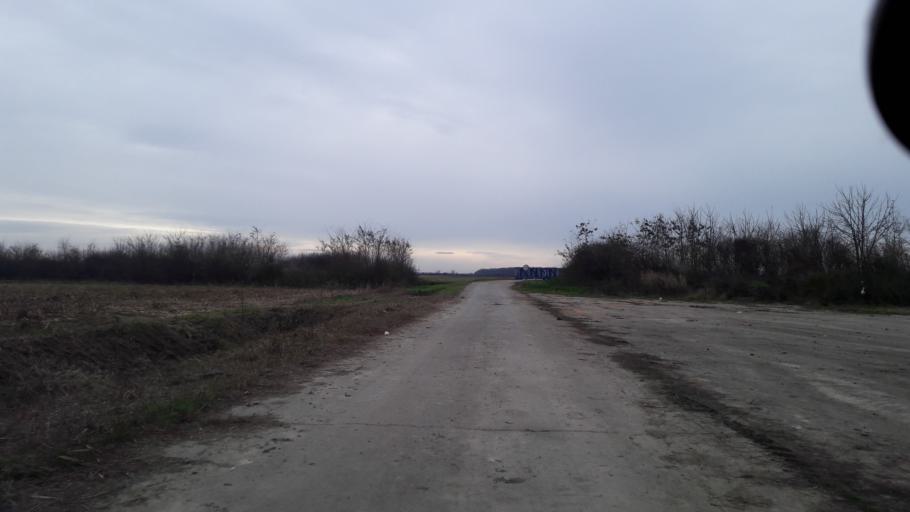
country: HR
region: Osjecko-Baranjska
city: Vladislavci
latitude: 45.4319
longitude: 18.5734
